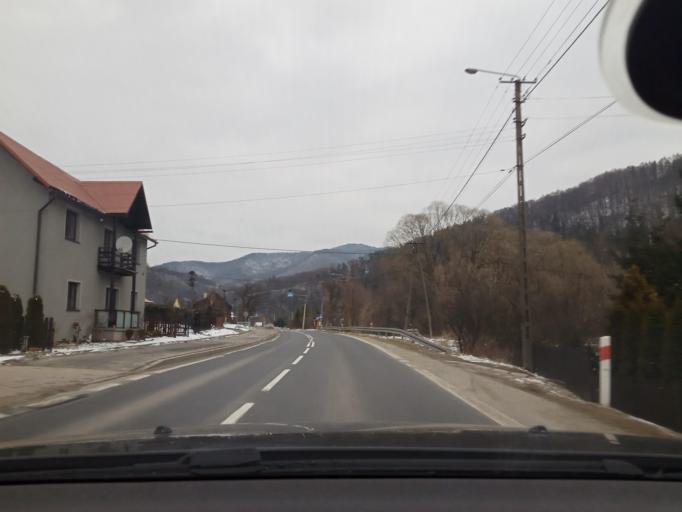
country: PL
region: Lesser Poland Voivodeship
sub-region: Powiat nowotarski
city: Kroscienko nad Dunajcem
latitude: 49.4589
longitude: 20.4268
